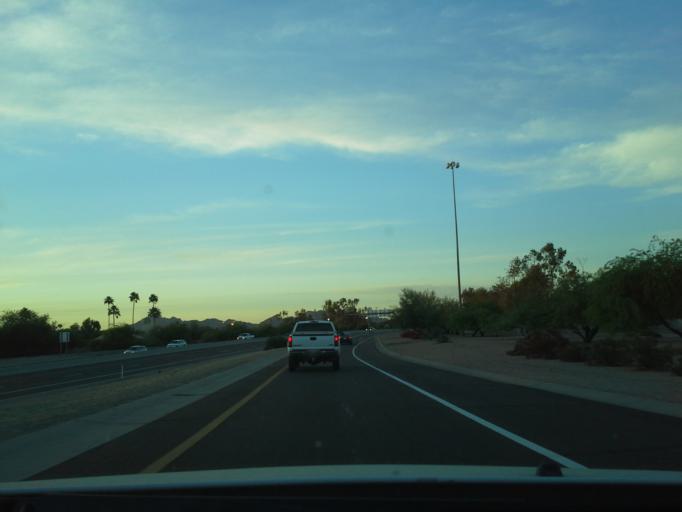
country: US
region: Arizona
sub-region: Maricopa County
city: Tempe Junction
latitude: 33.4605
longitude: -111.9827
